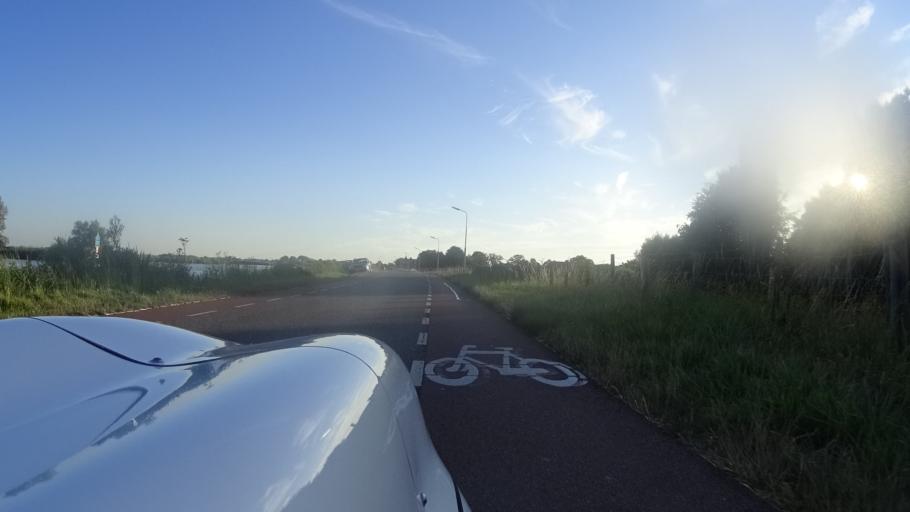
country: NL
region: South Holland
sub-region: Gemeente Kaag en Braassem
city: Leimuiden
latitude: 52.2429
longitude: 4.6918
